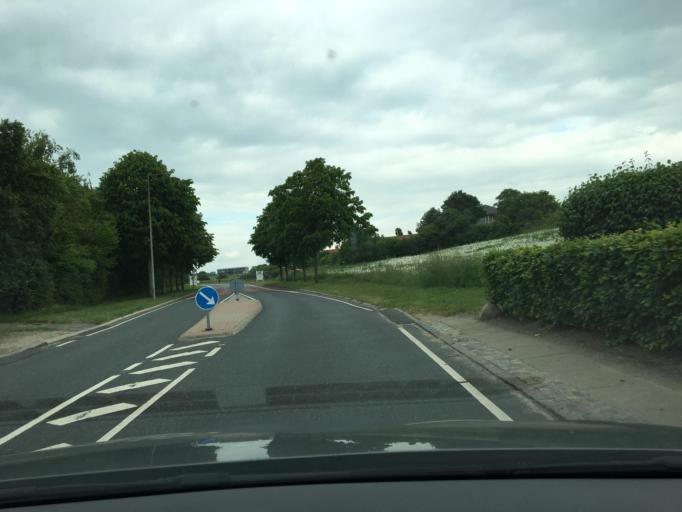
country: DK
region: South Denmark
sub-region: Assens Kommune
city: Assens
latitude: 55.2748
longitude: 9.8971
